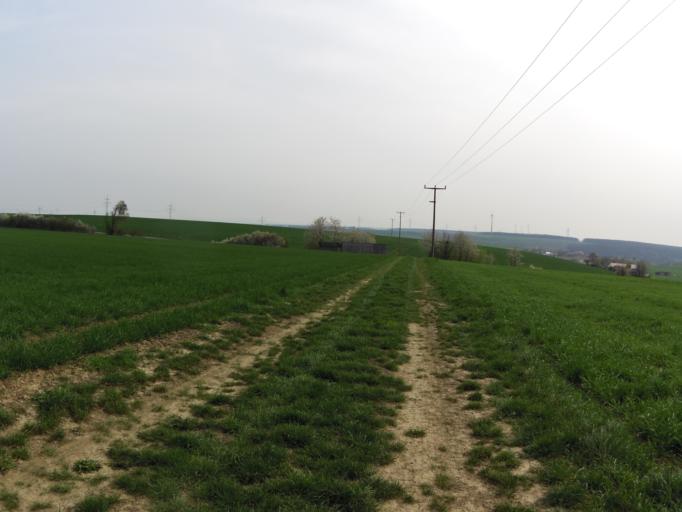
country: DE
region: Bavaria
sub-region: Regierungsbezirk Unterfranken
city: Theilheim
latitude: 49.7703
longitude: 10.0359
